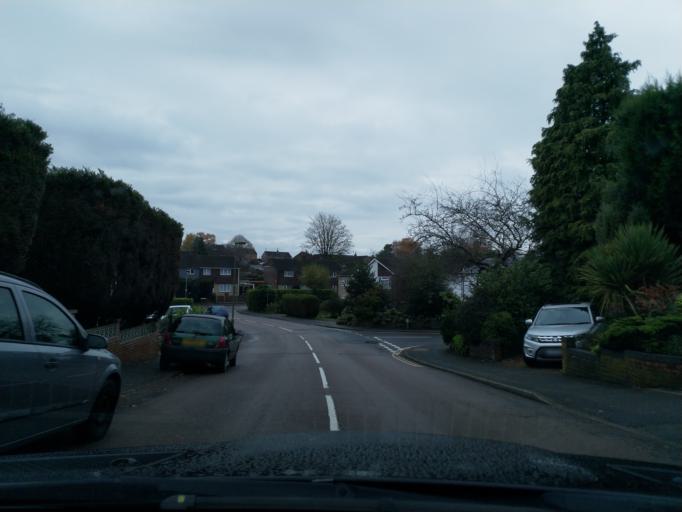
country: GB
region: England
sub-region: Surrey
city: Frimley
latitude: 51.3168
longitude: -0.7321
